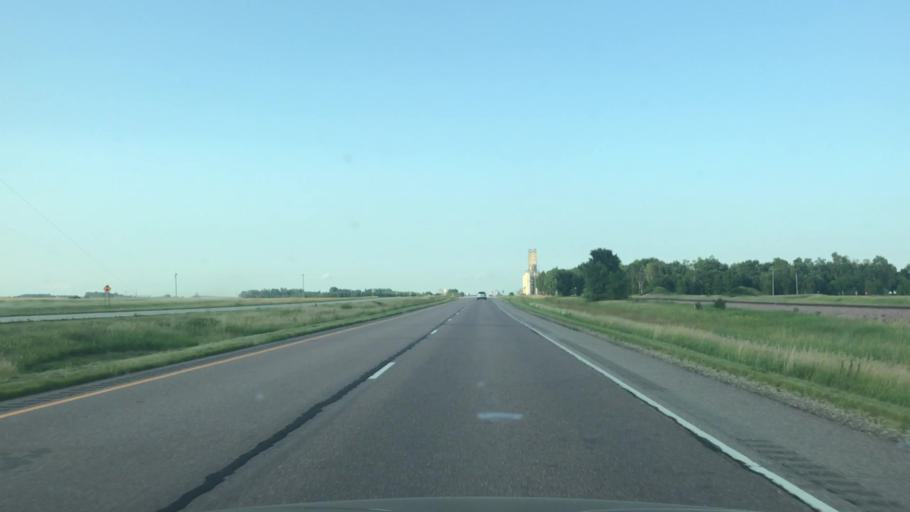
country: US
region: Minnesota
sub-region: Jackson County
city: Lakefield
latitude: 43.7615
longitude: -95.3745
